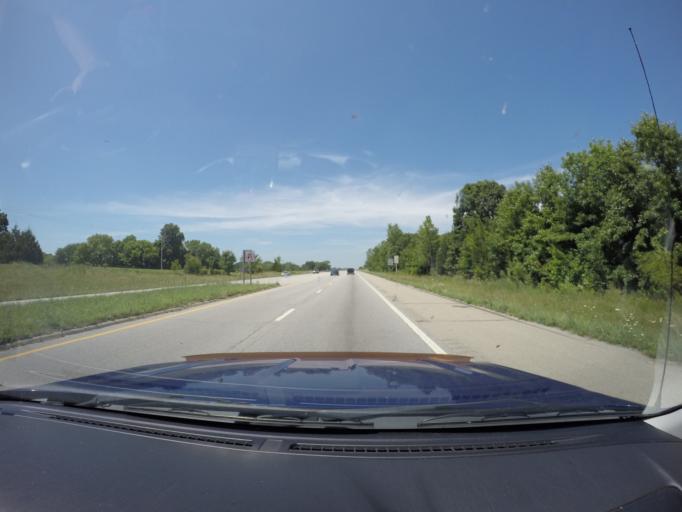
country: US
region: Kansas
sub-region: Wyandotte County
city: Bonner Springs
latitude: 39.1074
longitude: -94.8852
